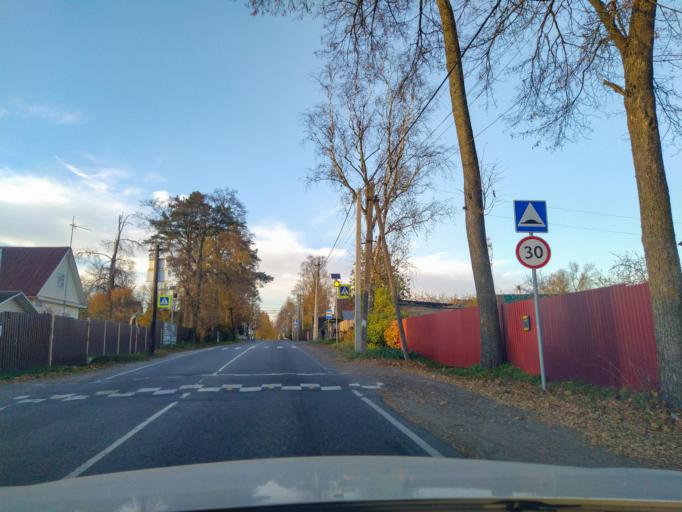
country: RU
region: Leningrad
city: Kobrinskoye
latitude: 59.4265
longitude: 30.1154
